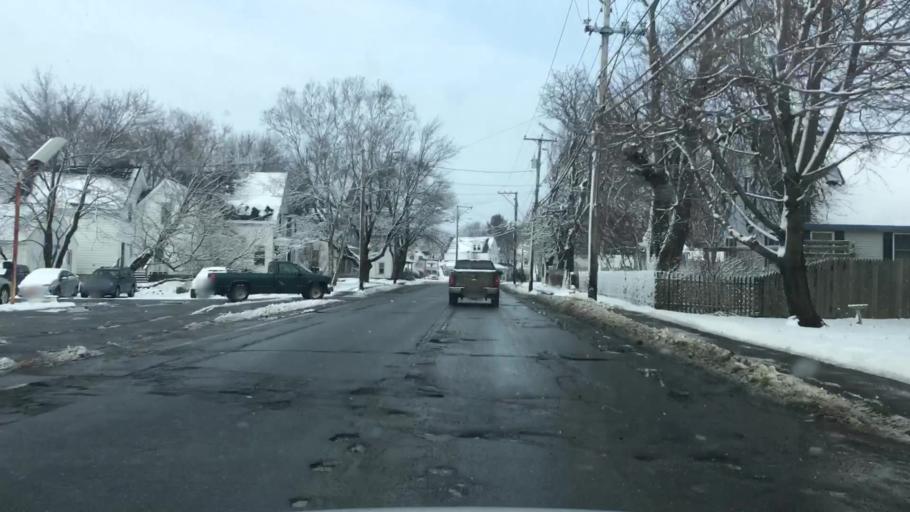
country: US
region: Maine
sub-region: Knox County
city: Rockland
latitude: 44.0967
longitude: -69.1107
